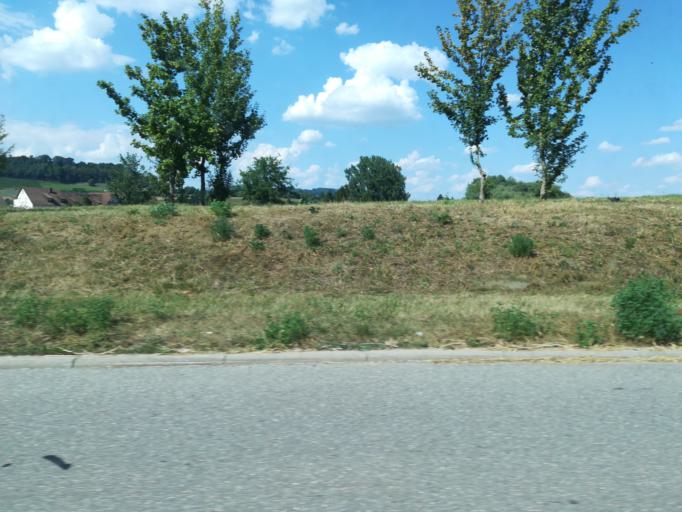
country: CH
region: Schaffhausen
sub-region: Bezirk Reiat
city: Thayngen
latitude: 47.7396
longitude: 8.7374
